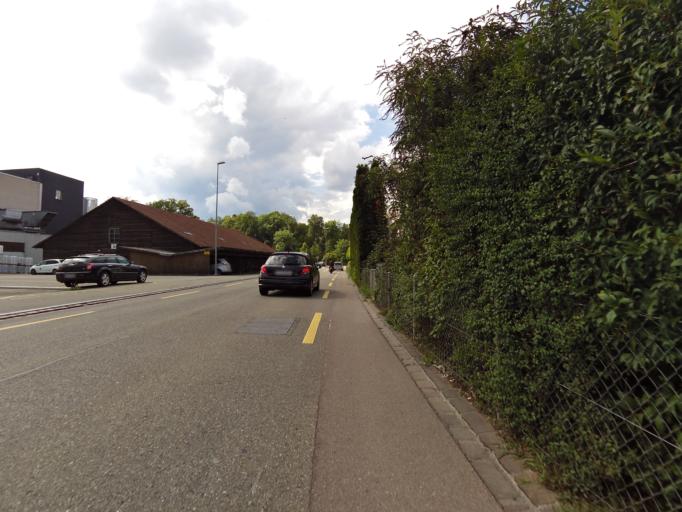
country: CH
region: Thurgau
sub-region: Frauenfeld District
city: Frauenfeld
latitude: 47.5642
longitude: 8.8987
